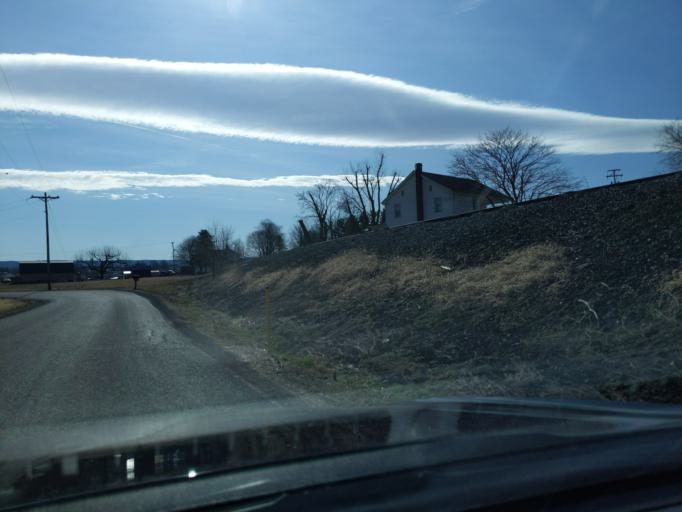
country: US
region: Pennsylvania
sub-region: Blair County
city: Martinsburg
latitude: 40.3121
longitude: -78.3427
